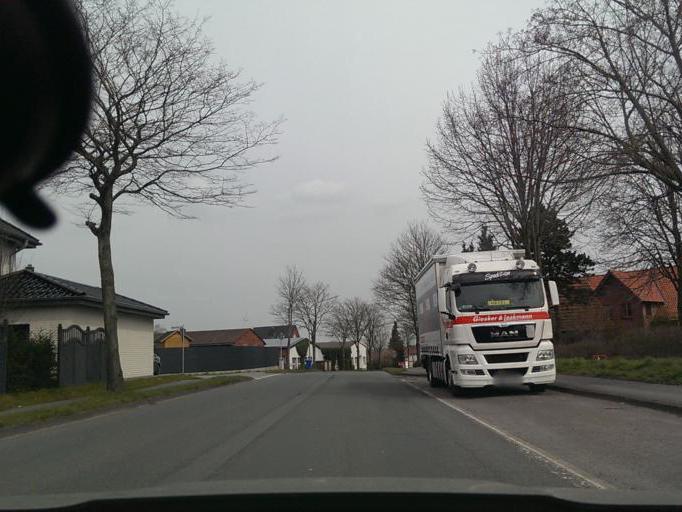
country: DE
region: North Rhine-Westphalia
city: Rietberg
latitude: 51.7529
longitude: 8.4648
